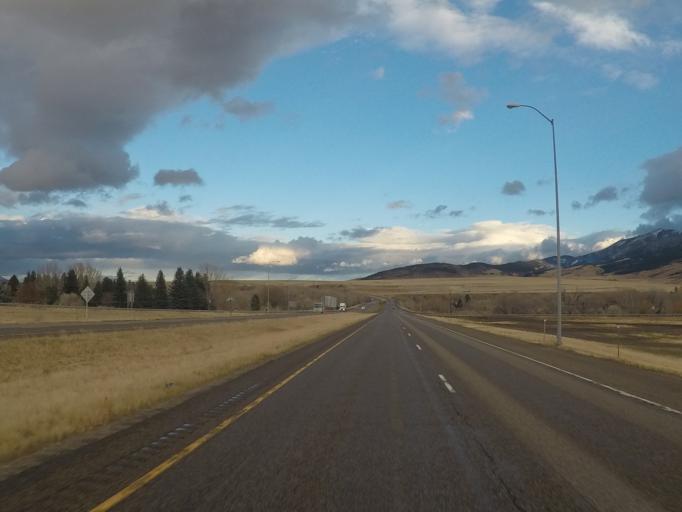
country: US
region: Montana
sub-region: Park County
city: Livingston
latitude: 45.6443
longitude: -110.5713
